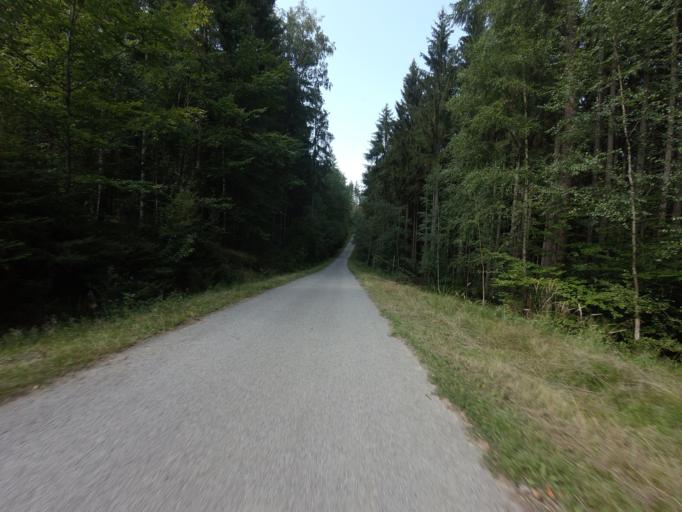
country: CZ
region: Jihocesky
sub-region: Okres Ceske Budejovice
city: Hluboka nad Vltavou
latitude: 49.1027
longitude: 14.4621
